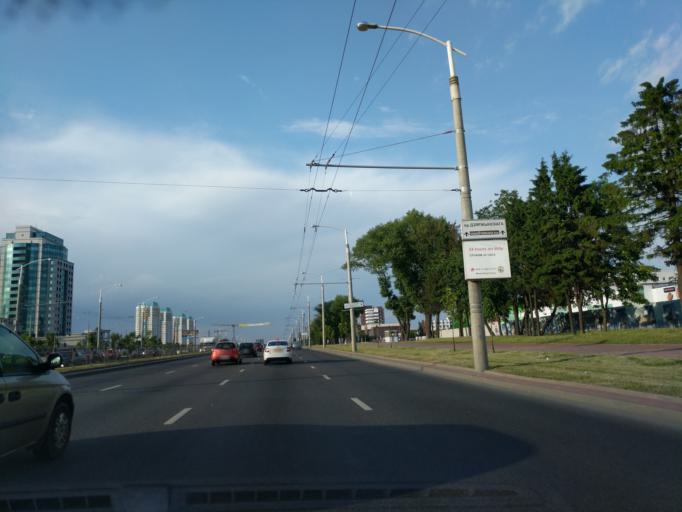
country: BY
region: Minsk
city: Novoye Medvezhino
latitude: 53.8587
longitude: 27.4793
